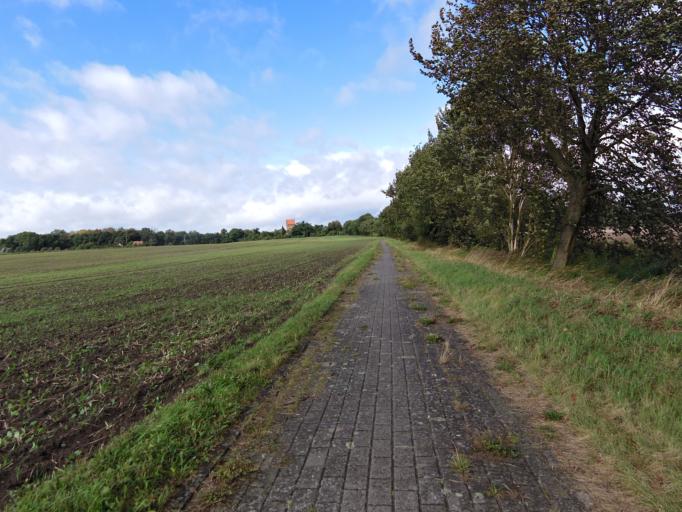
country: DE
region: Saxony-Anhalt
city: Hohenberg-Krusemark
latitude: 52.7496
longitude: 12.0140
